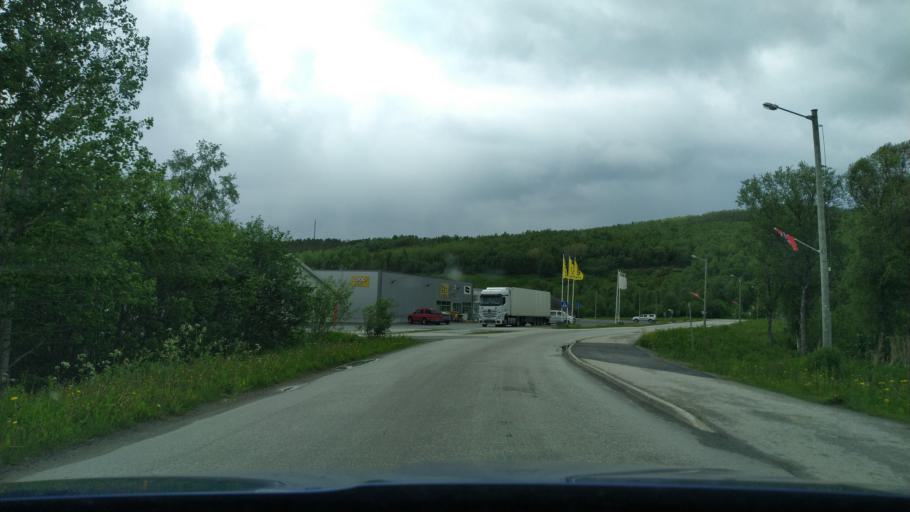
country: NO
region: Troms
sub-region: Dyroy
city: Brostadbotn
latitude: 69.0910
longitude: 17.6970
